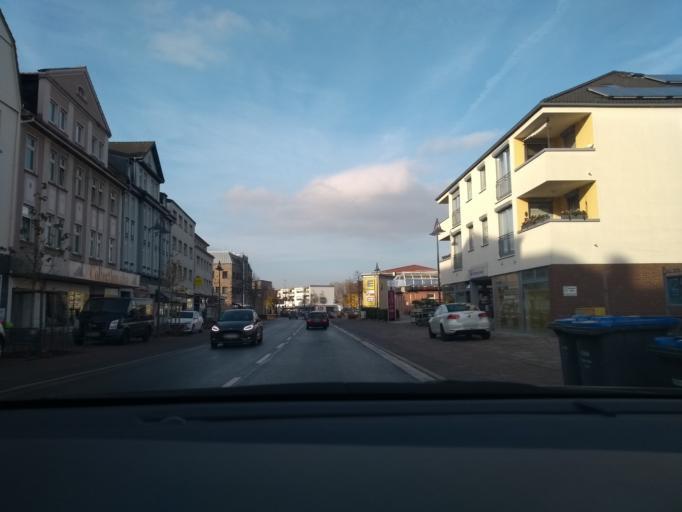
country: DE
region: North Rhine-Westphalia
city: Selm
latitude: 51.6889
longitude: 7.4662
